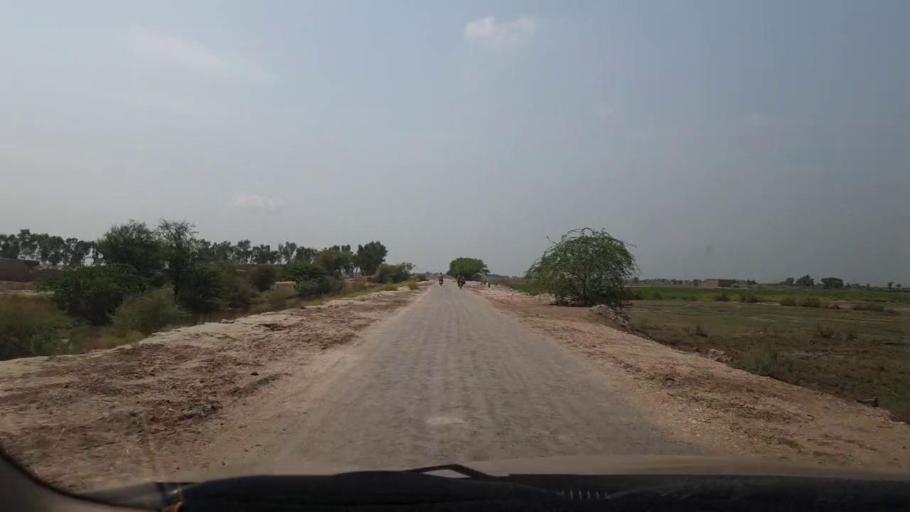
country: PK
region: Sindh
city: Goth Garelo
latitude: 27.5065
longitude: 68.1139
